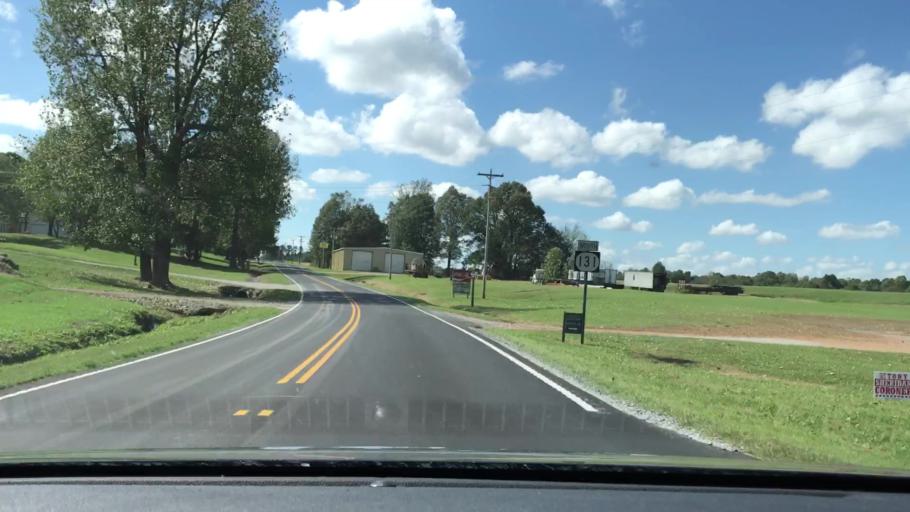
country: US
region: Kentucky
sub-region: McCracken County
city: Reidland
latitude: 36.8838
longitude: -88.5547
